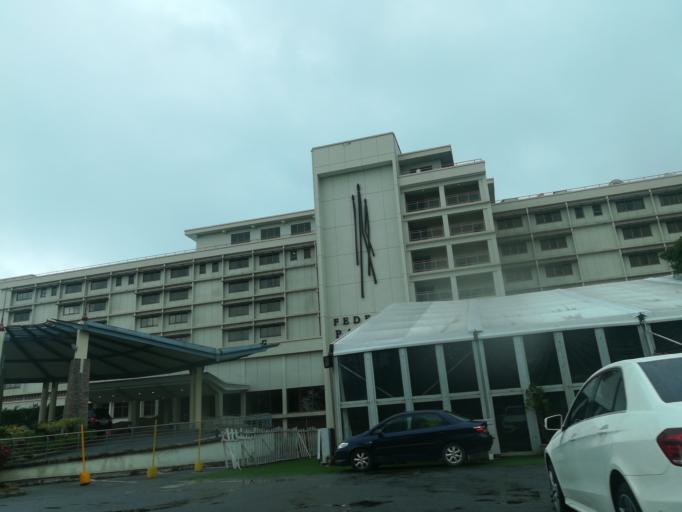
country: NG
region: Lagos
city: Lagos
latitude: 6.4310
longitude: 3.4077
